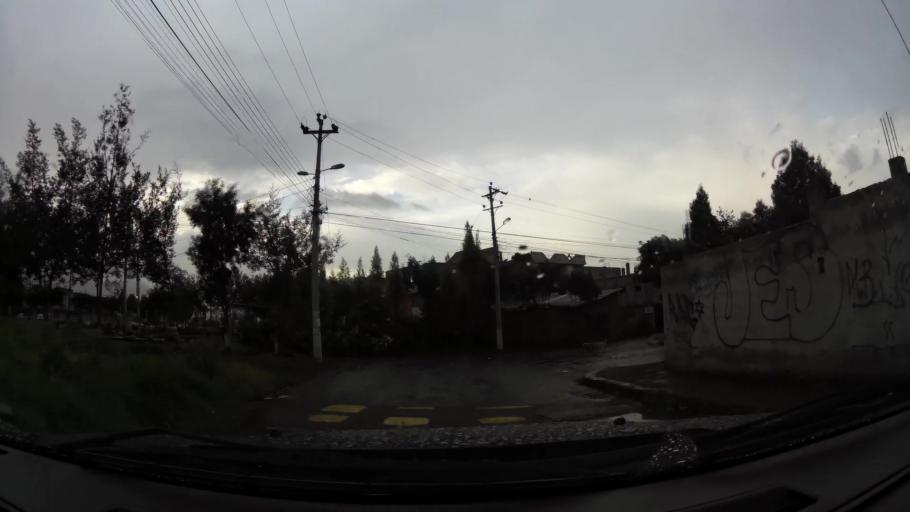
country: EC
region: Pichincha
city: Quito
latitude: -0.3109
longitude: -78.5517
